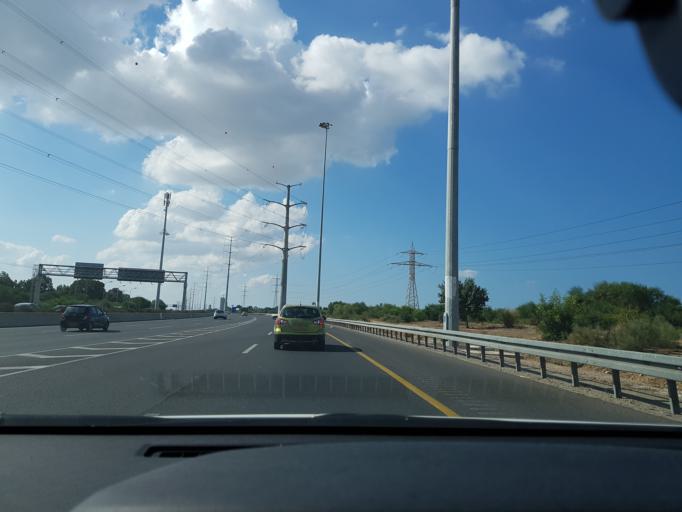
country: IL
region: Central District
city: Bet Dagan
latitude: 31.9973
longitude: 34.8010
